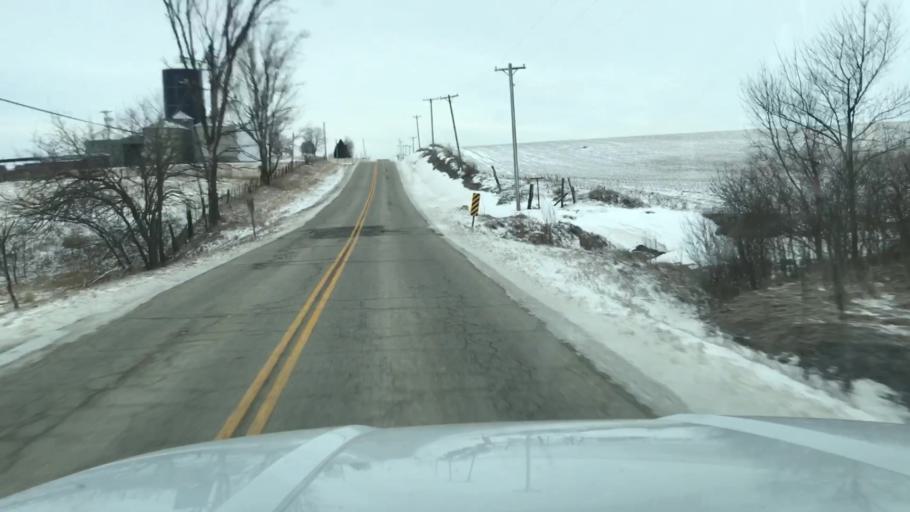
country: US
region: Missouri
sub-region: Andrew County
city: Savannah
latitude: 40.0250
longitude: -94.9508
